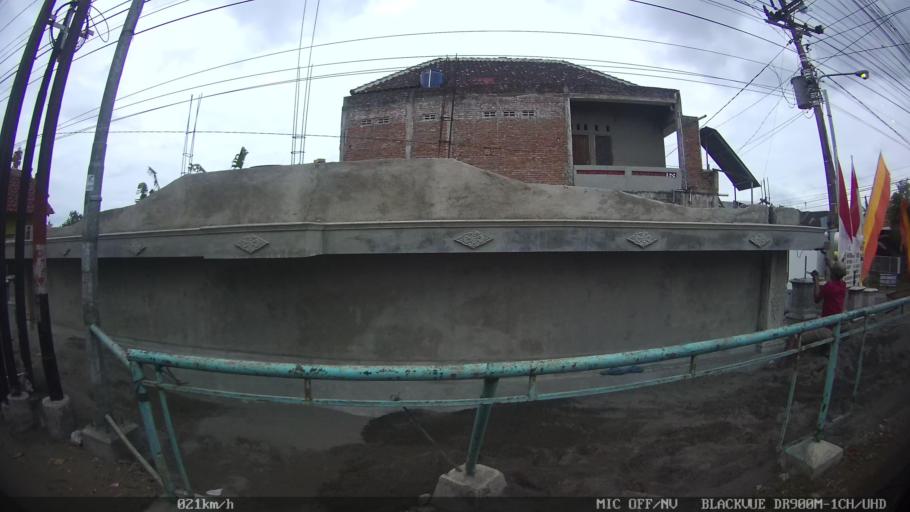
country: ID
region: Daerah Istimewa Yogyakarta
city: Sewon
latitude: -7.8391
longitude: 110.4115
